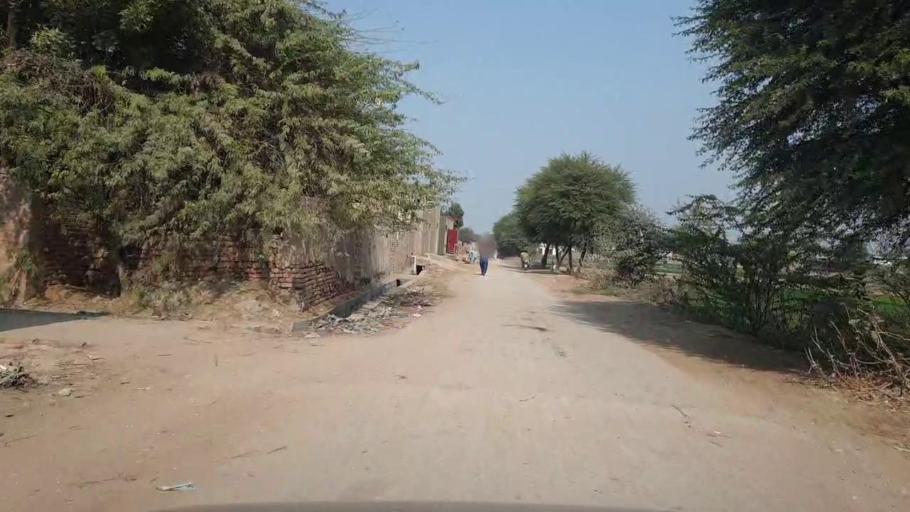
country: PK
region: Sindh
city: Bhit Shah
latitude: 25.7968
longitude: 68.4925
